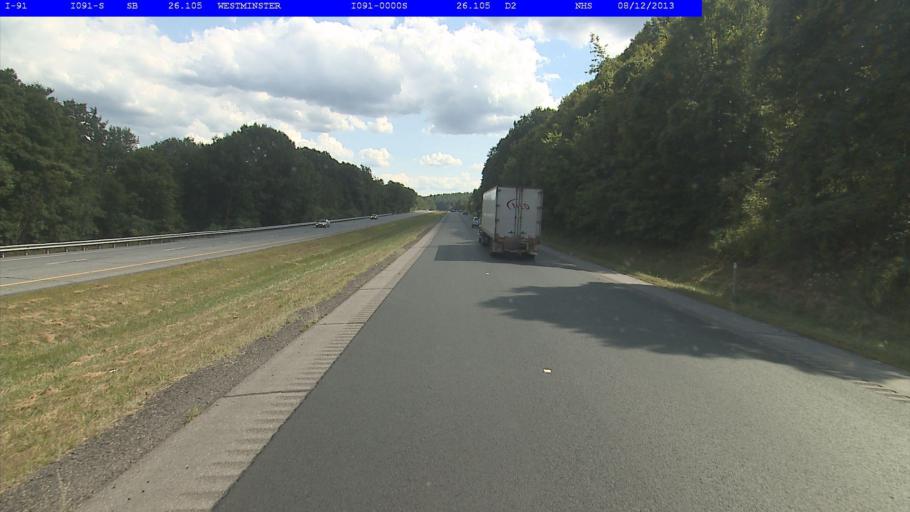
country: US
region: Vermont
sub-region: Windham County
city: Bellows Falls
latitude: 43.0571
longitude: -72.4704
